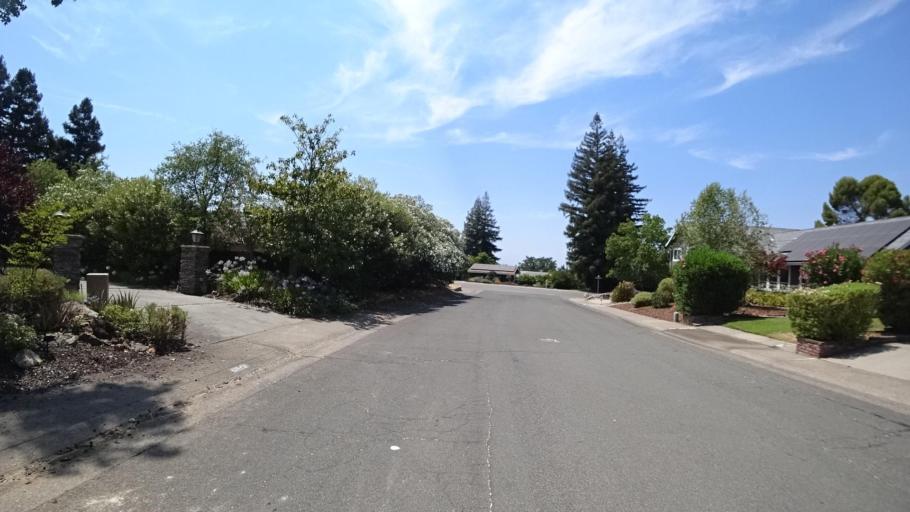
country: US
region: California
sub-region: Placer County
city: Rocklin
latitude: 38.8005
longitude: -121.2461
